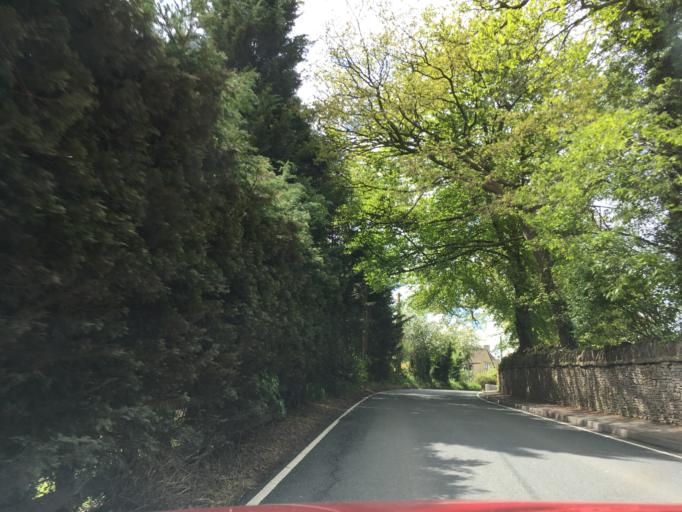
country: GB
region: England
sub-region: Gloucestershire
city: Stonehouse
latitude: 51.7355
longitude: -2.2738
